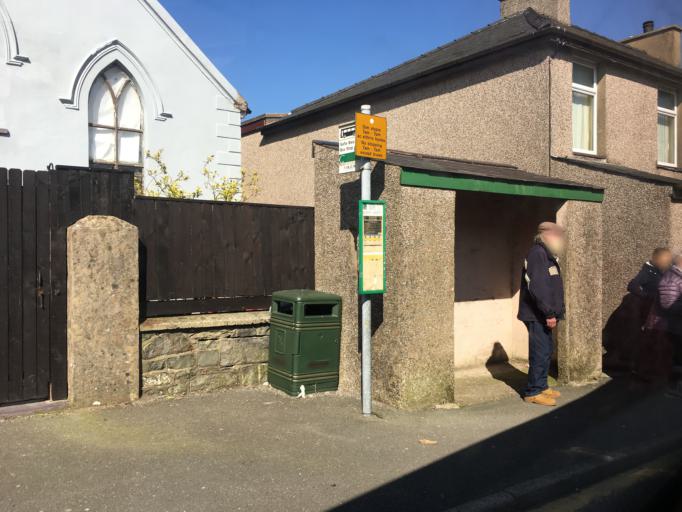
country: GB
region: Wales
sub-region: Gwynedd
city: Llanwnda
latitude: 53.0411
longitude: -4.2838
